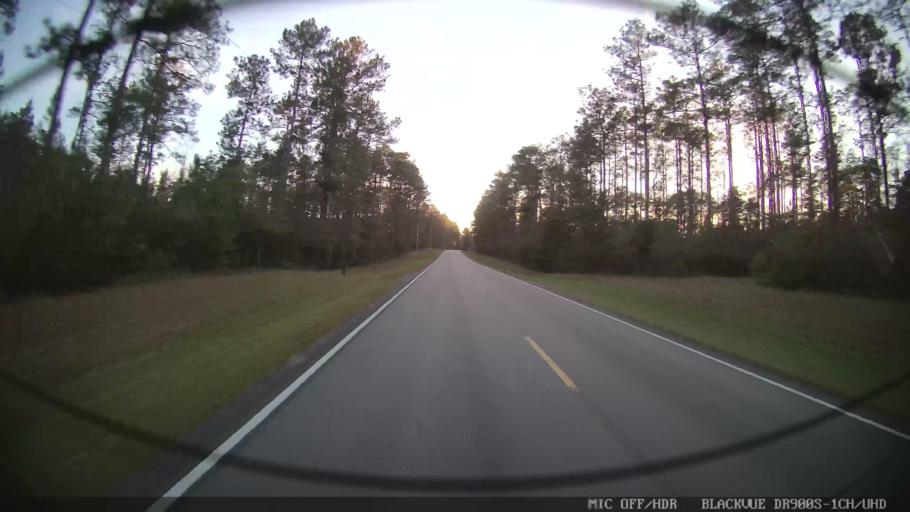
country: US
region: Mississippi
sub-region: Stone County
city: Wiggins
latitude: 31.0389
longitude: -89.2150
